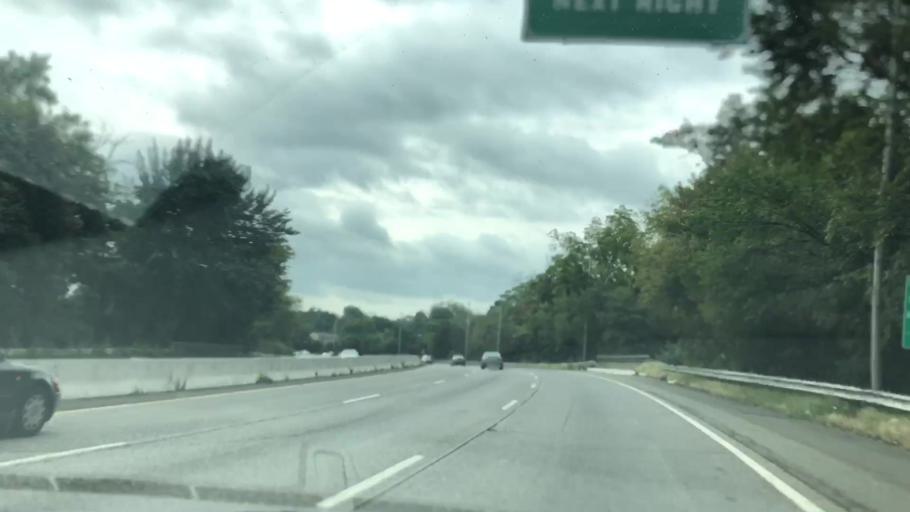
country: US
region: New Jersey
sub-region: Bergen County
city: Lyndhurst
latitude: 40.8196
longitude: -74.1354
